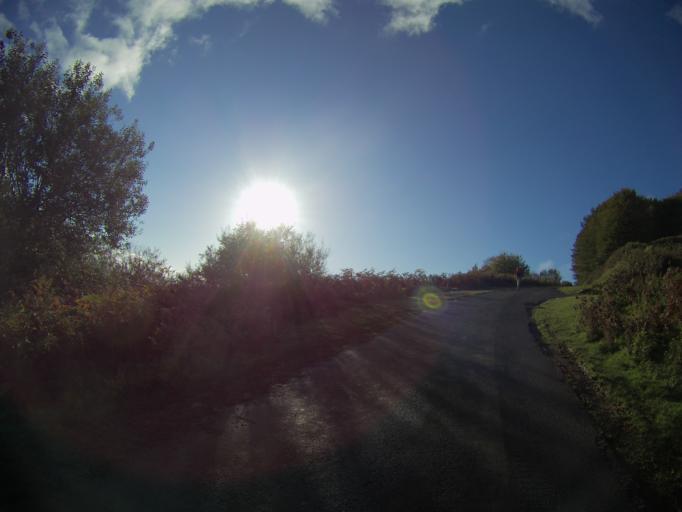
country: FR
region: Aquitaine
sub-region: Departement des Pyrenees-Atlantiques
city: Saint-Jean-Pied-de-Port
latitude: 43.1177
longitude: -1.2382
